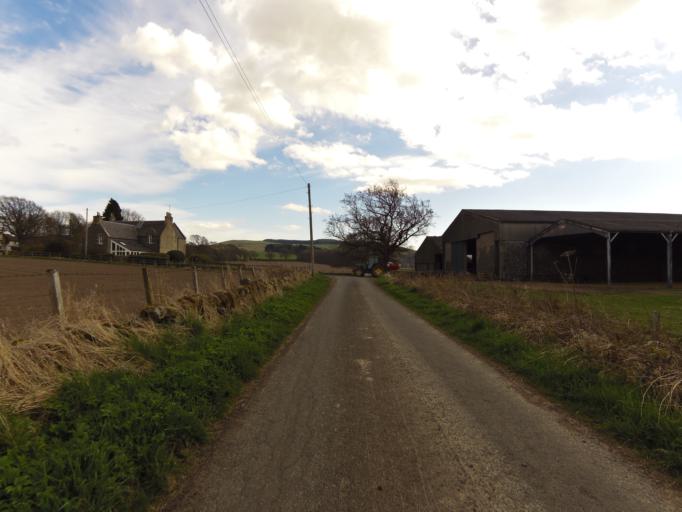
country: GB
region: Scotland
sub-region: Fife
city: Newburgh
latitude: 56.3327
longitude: -3.2350
